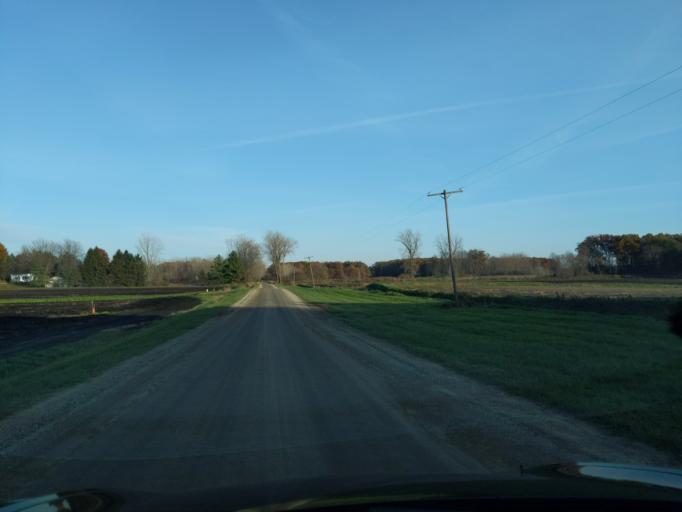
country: US
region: Michigan
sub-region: Clinton County
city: Bath
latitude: 42.7986
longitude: -84.4972
